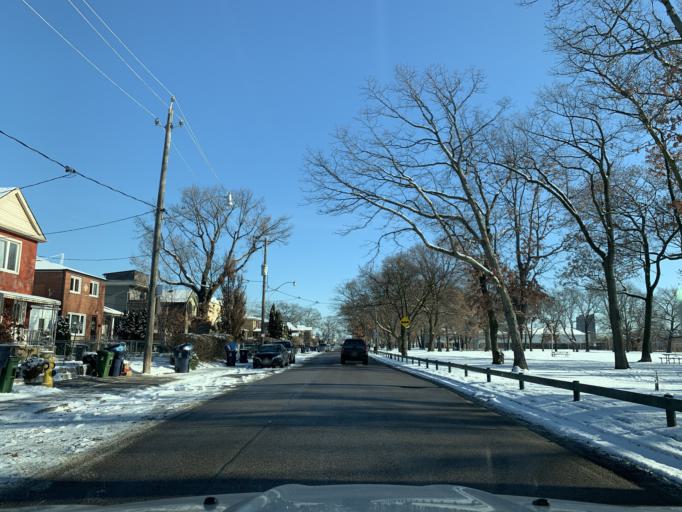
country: CA
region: Ontario
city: Toronto
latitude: 43.6684
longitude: -79.4810
